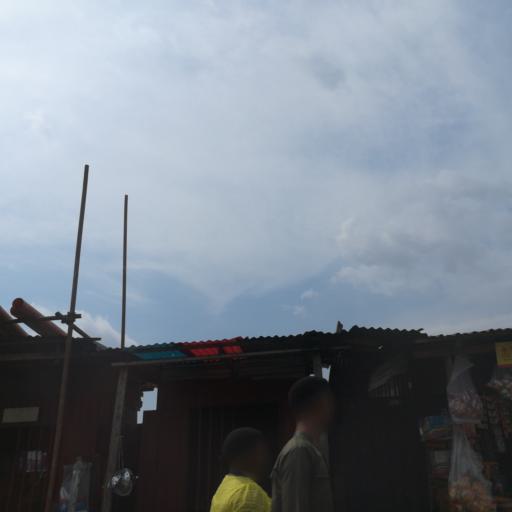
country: NG
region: Rivers
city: Port Harcourt
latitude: 4.8700
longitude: 7.0222
